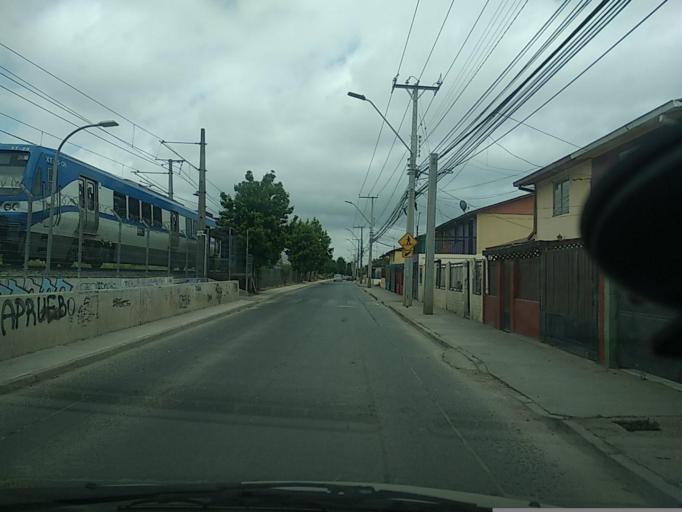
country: CL
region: Valparaiso
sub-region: Provincia de Marga Marga
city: Villa Alemana
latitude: -33.0415
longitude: -71.3627
